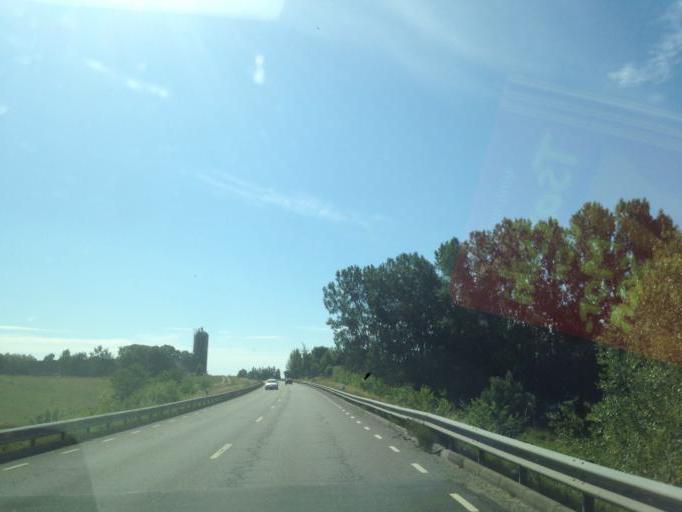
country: SE
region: Skane
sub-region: Simrishamns Kommun
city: Kivik
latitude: 55.6275
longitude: 14.2566
